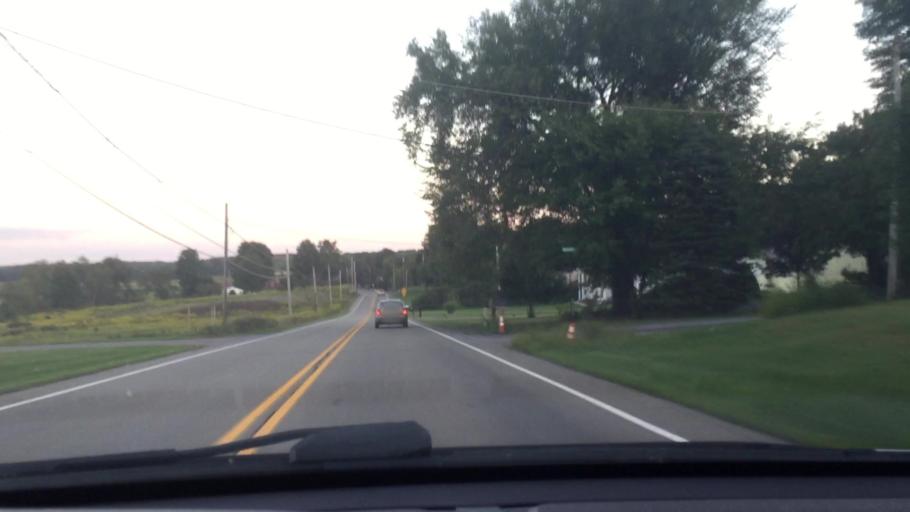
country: US
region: Pennsylvania
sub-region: Mercer County
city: Grove City
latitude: 41.1383
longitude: -80.0779
